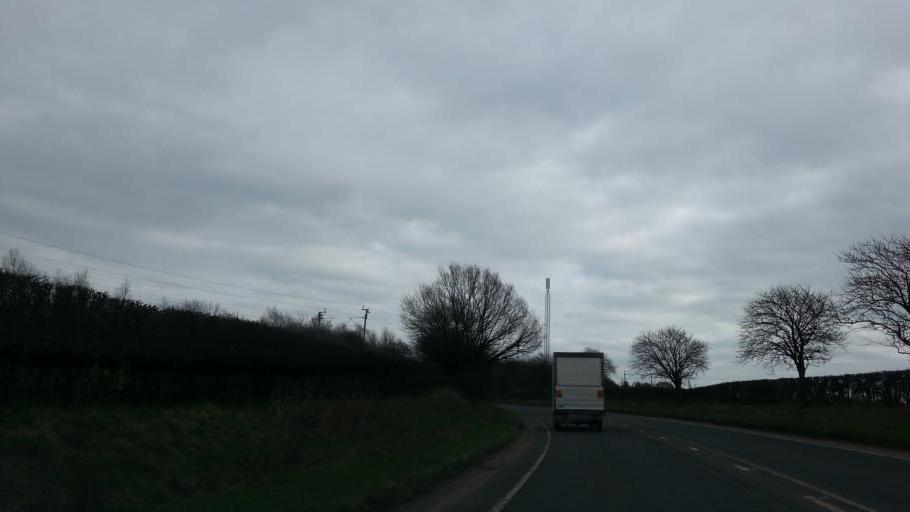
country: GB
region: England
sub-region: Staffordshire
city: Stone
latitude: 52.8803
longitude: -2.1135
